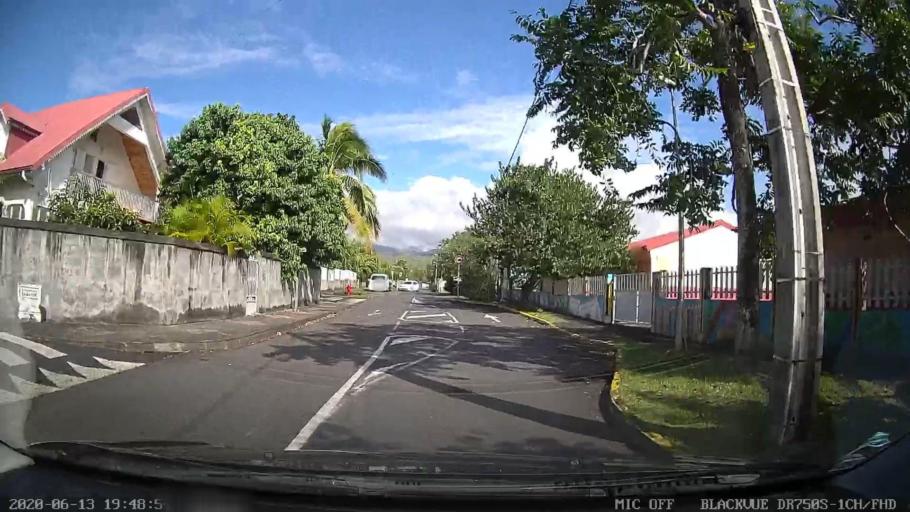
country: RE
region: Reunion
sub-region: Reunion
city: Bras-Panon
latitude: -21.0033
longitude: 55.6907
